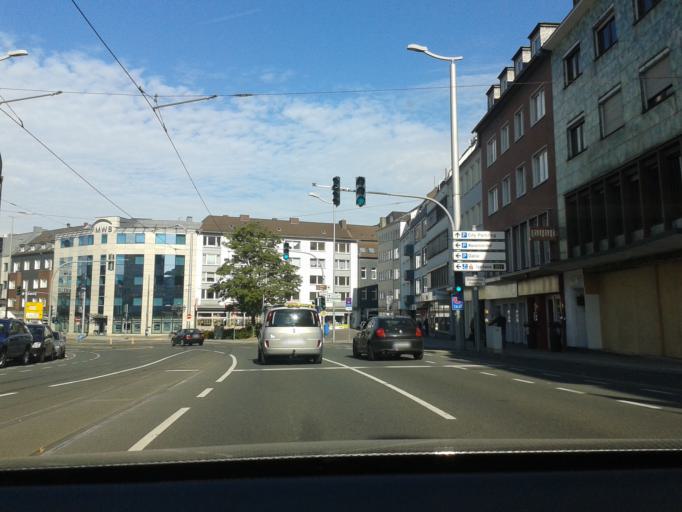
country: DE
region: North Rhine-Westphalia
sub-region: Regierungsbezirk Dusseldorf
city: Muelheim (Ruhr)
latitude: 51.4255
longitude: 6.8819
